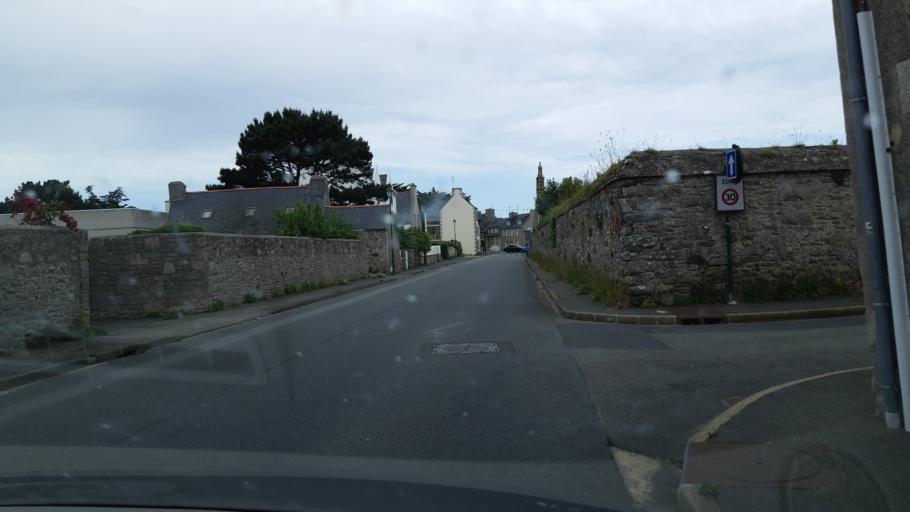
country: FR
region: Brittany
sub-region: Departement du Finistere
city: Roscoff
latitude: 48.7196
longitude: -3.9854
